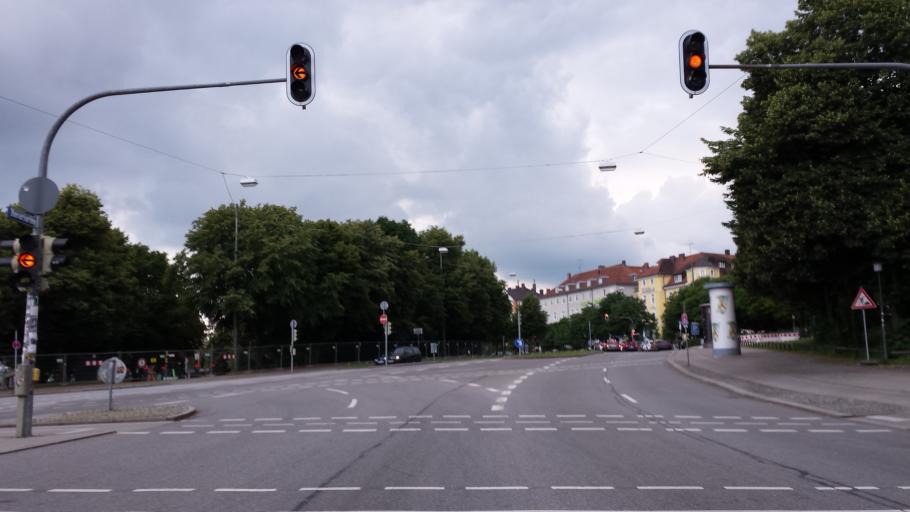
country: DE
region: Bavaria
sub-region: Upper Bavaria
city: Munich
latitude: 48.1364
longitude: 11.5493
